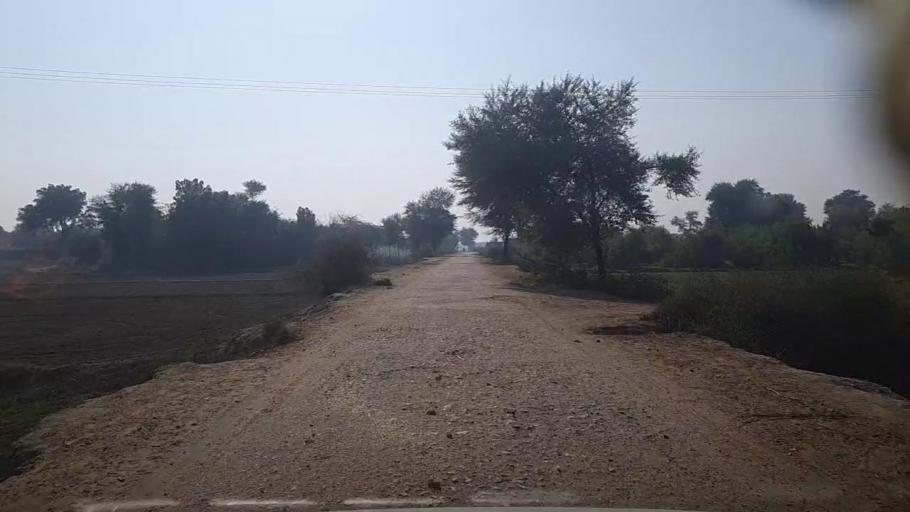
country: PK
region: Sindh
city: Kandiari
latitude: 26.9885
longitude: 68.4694
